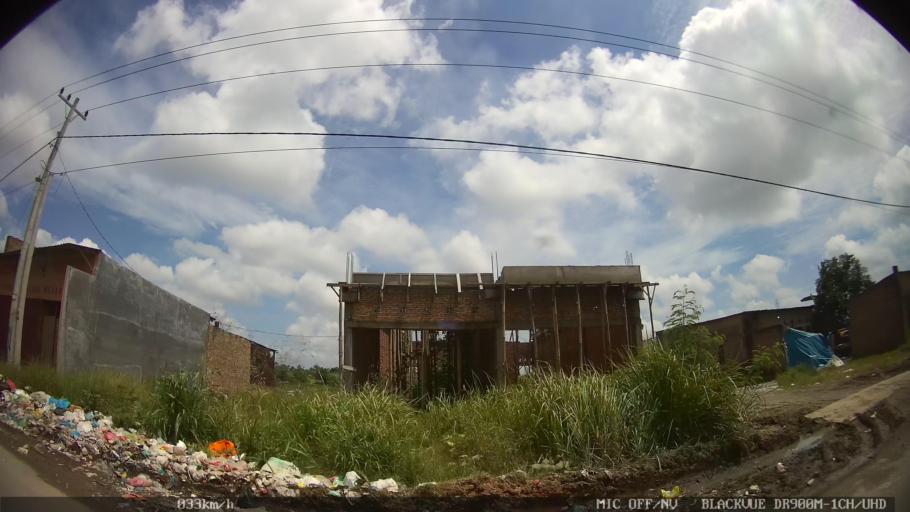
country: ID
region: North Sumatra
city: Percut
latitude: 3.6201
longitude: 98.7723
